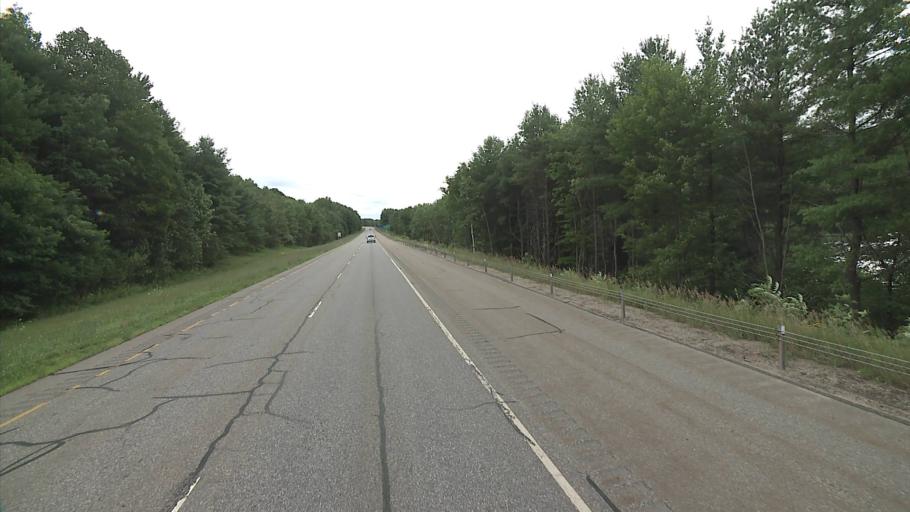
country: US
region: Connecticut
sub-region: Litchfield County
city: Winsted
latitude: 41.8992
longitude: -73.0674
